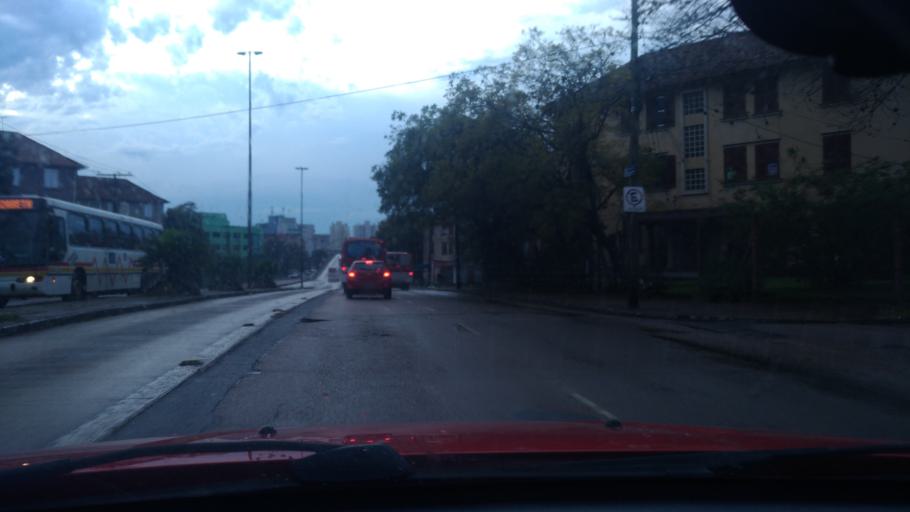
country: BR
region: Rio Grande do Sul
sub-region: Porto Alegre
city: Porto Alegre
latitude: -30.0115
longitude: -51.1740
